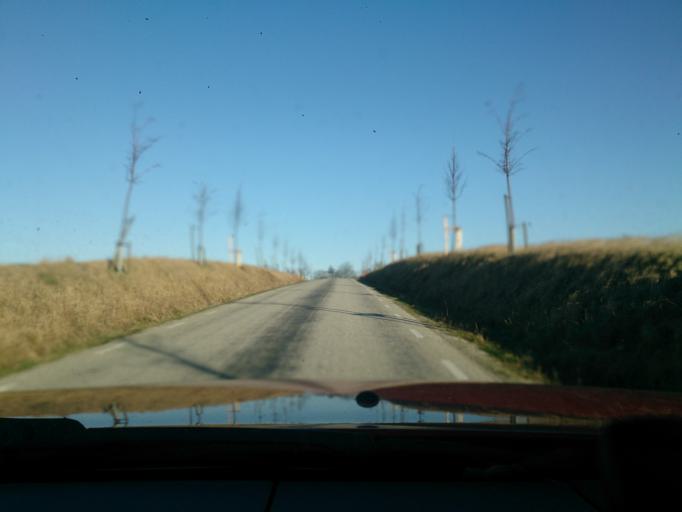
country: SE
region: Skane
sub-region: Skurups Kommun
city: Rydsgard
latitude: 55.4416
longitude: 13.6870
